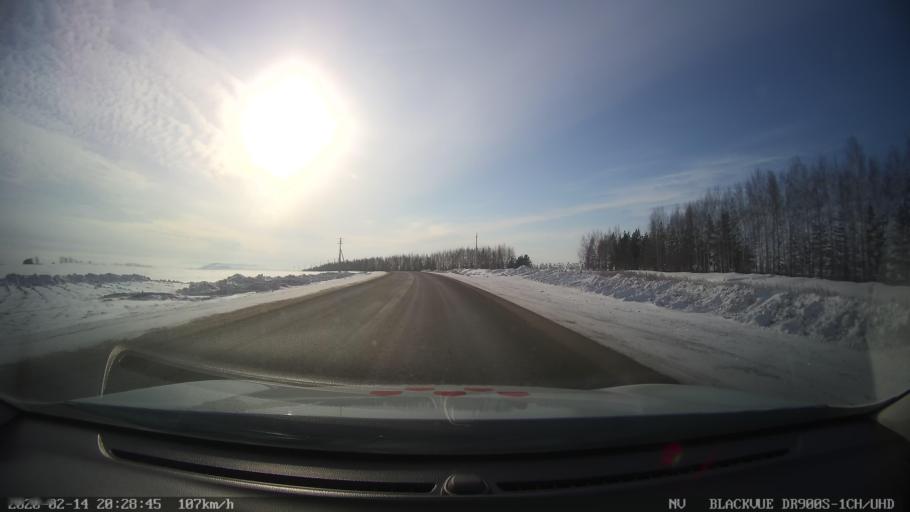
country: RU
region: Tatarstan
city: Stolbishchi
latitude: 55.4587
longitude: 48.9774
